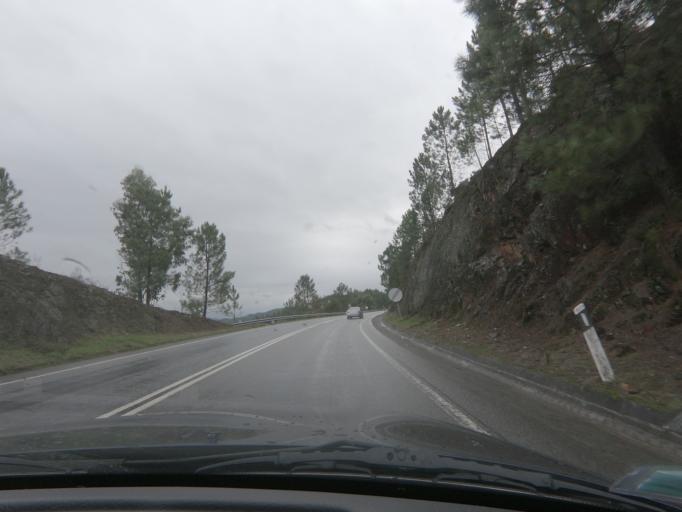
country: PT
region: Porto
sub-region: Amarante
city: Amarante
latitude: 41.3262
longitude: -8.0420
